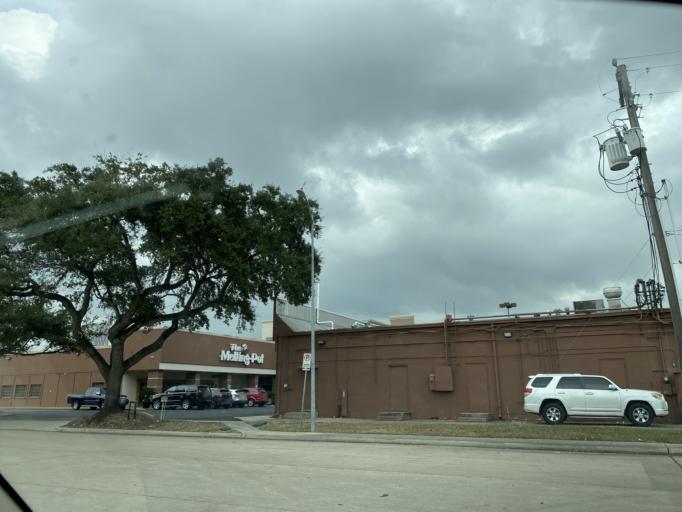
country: US
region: Texas
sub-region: Harris County
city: Hunters Creek Village
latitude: 29.7386
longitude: -95.4917
